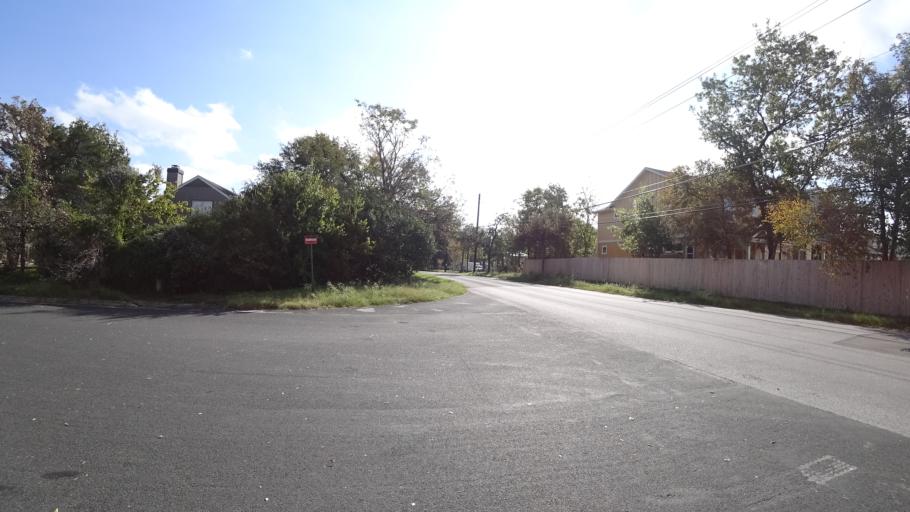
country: US
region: Texas
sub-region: Travis County
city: Shady Hollow
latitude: 30.1936
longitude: -97.8285
